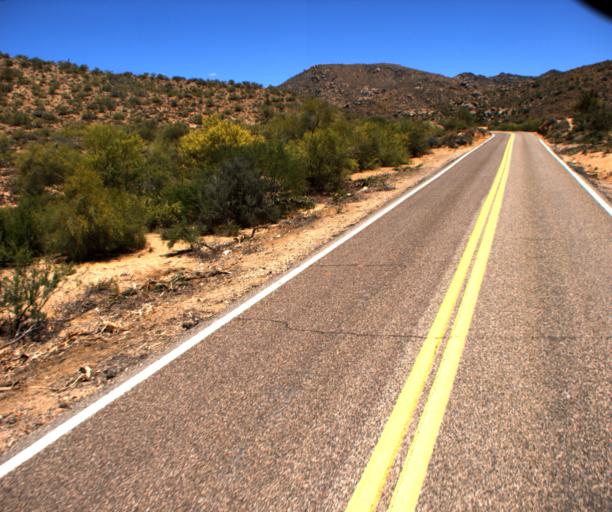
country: US
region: Arizona
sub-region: Yavapai County
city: Bagdad
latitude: 34.4533
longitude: -112.9869
